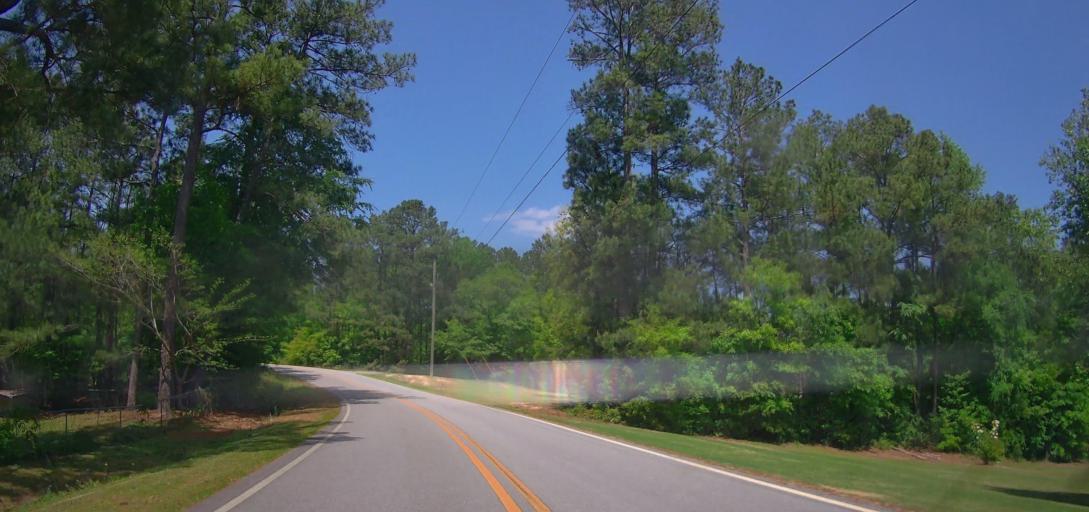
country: US
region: Georgia
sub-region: Bibb County
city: Macon
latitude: 32.9256
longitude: -83.5925
